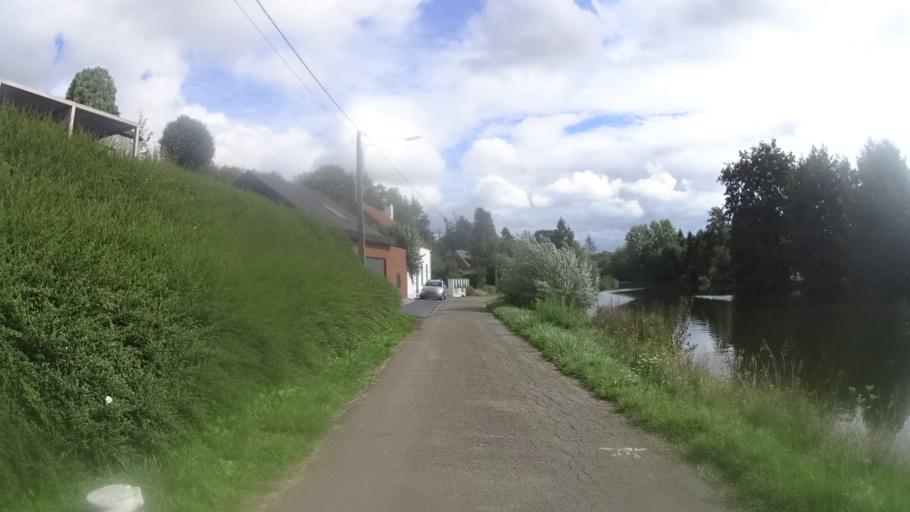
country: BE
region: Wallonia
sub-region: Province du Hainaut
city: Merbes-le-Chateau
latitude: 50.3186
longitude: 4.1803
